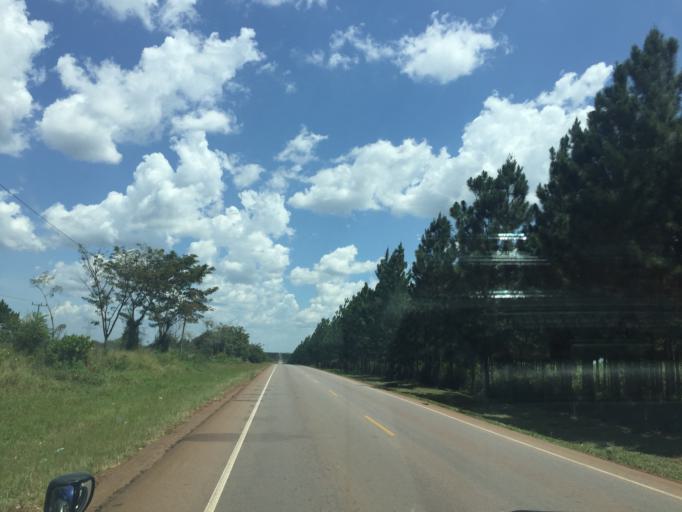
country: UG
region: Central Region
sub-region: Nakasongola District
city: Nakasongola
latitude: 1.3760
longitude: 32.3454
